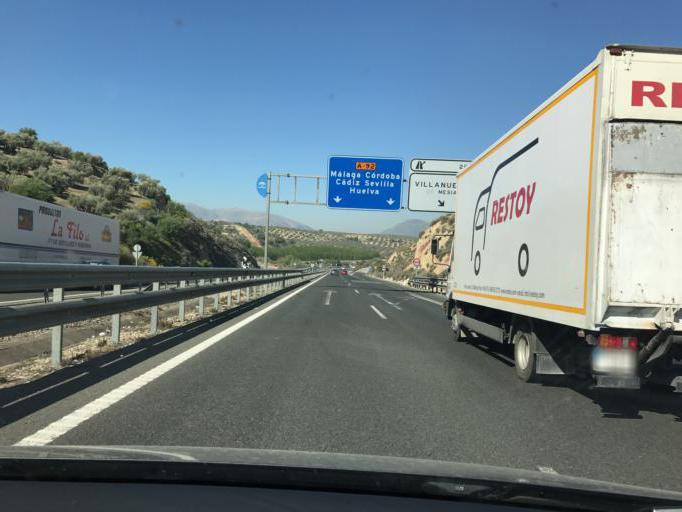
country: ES
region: Andalusia
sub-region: Provincia de Granada
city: Villanueva de Mesia
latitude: 37.1936
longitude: -3.9931
